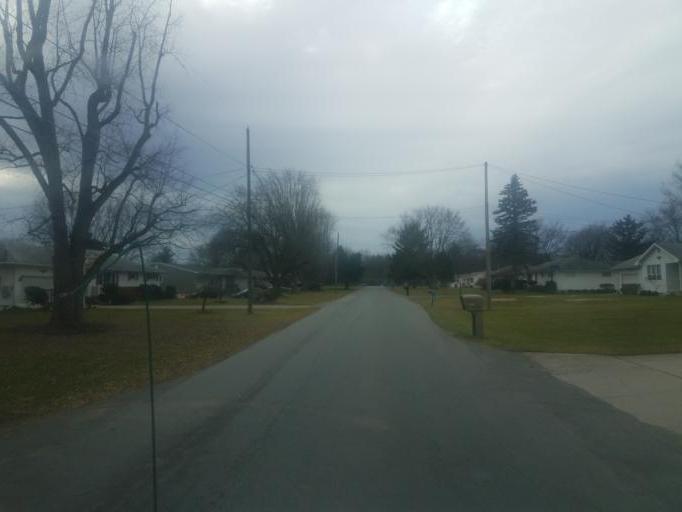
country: US
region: Ohio
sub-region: Marion County
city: Marion
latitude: 40.5702
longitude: -83.0862
